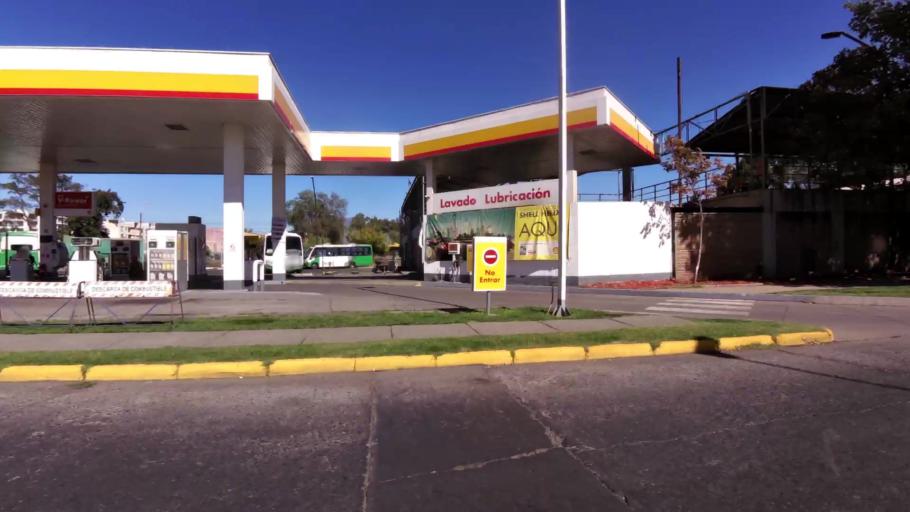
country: CL
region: O'Higgins
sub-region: Provincia de Cachapoal
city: Rancagua
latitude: -34.1648
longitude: -70.7506
